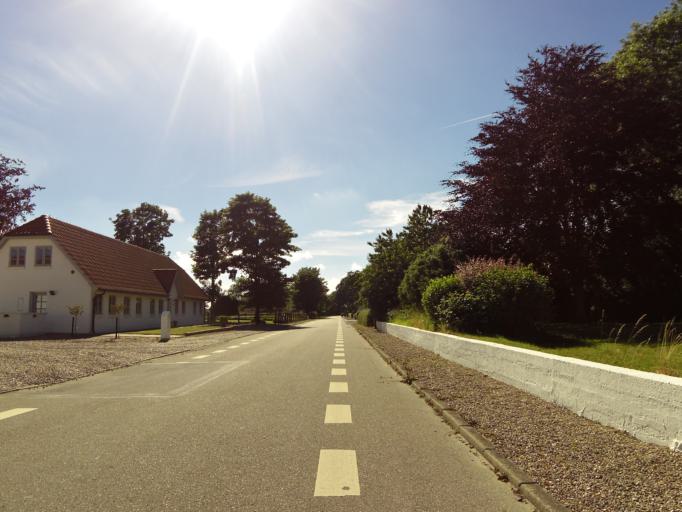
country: DK
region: South Denmark
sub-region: Aabenraa Kommune
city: Rodekro
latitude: 55.0659
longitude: 9.2573
